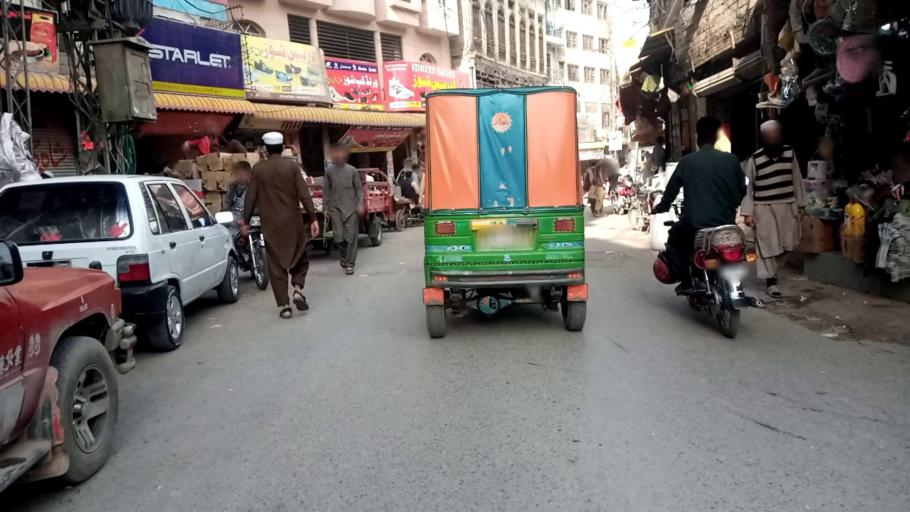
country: PK
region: Khyber Pakhtunkhwa
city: Peshawar
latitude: 34.0084
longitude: 71.5726
